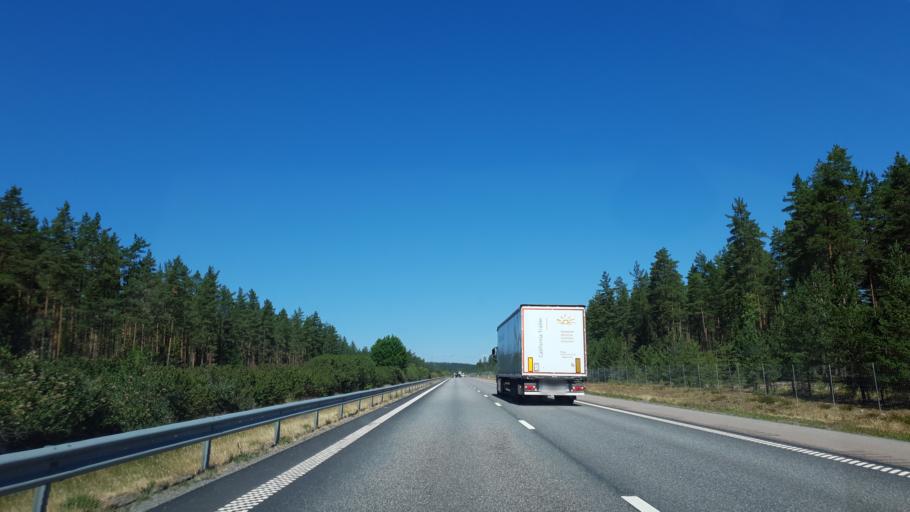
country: SE
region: Joenkoeping
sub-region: Vaggeryds Kommun
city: Skillingaryd
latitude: 57.3633
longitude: 14.1050
